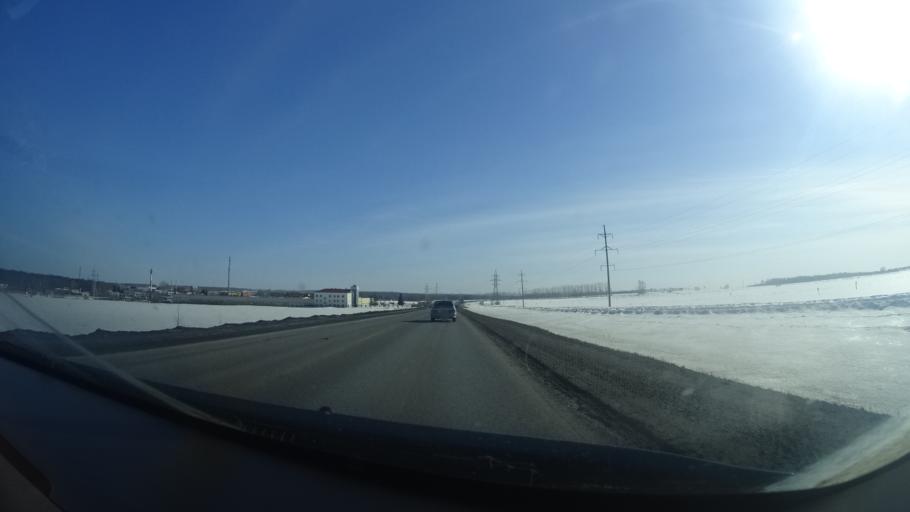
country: RU
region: Bashkortostan
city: Mikhaylovka
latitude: 54.8342
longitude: 55.8088
